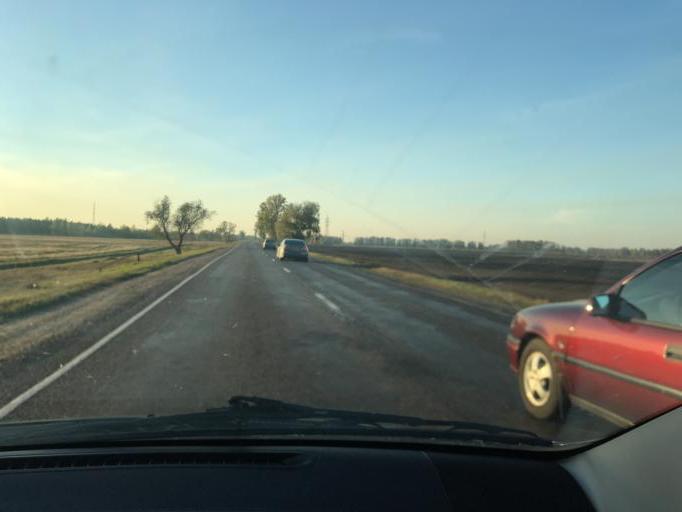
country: BY
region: Brest
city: Pinsk
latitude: 52.0675
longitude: 26.1868
